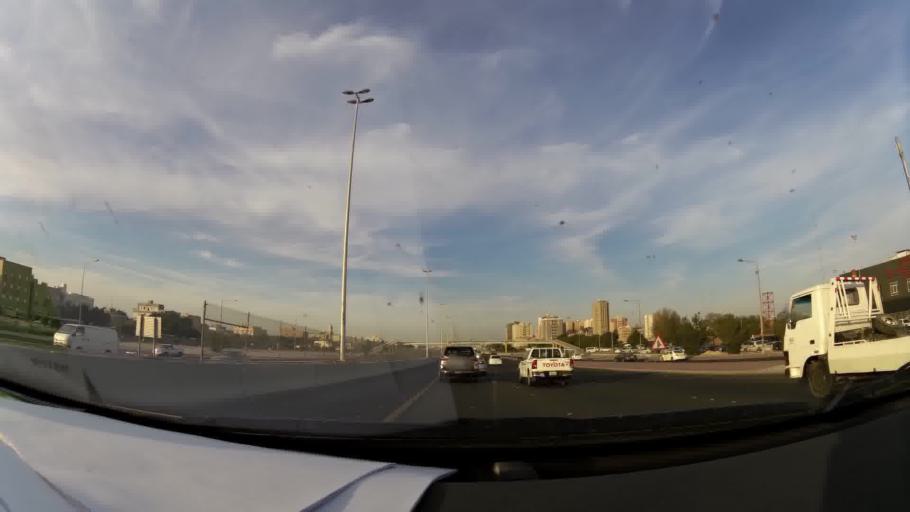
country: KW
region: Al Ahmadi
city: Al Manqaf
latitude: 29.0953
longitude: 48.1166
